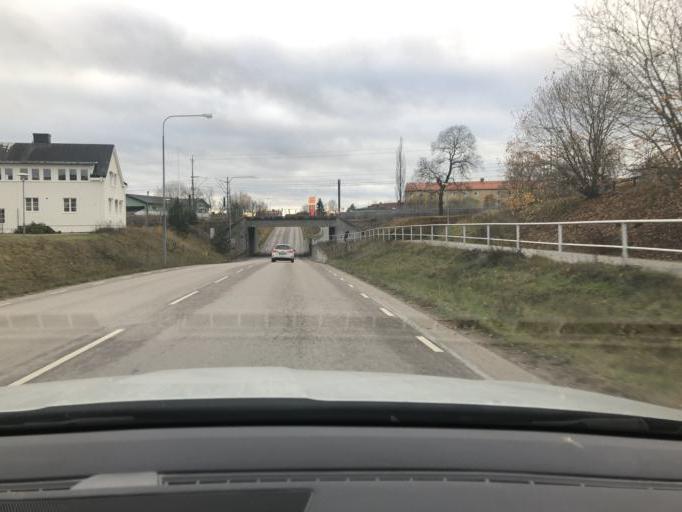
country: SE
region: Uppsala
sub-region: Tierps Kommun
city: Tierp
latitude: 60.3432
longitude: 17.5214
